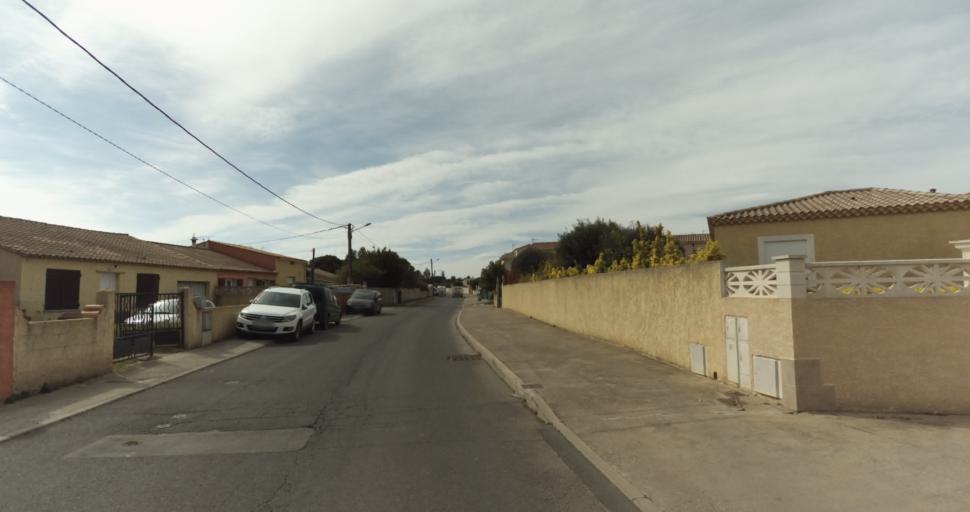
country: FR
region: Languedoc-Roussillon
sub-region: Departement de l'Herault
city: Marseillan
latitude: 43.3350
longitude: 3.5297
